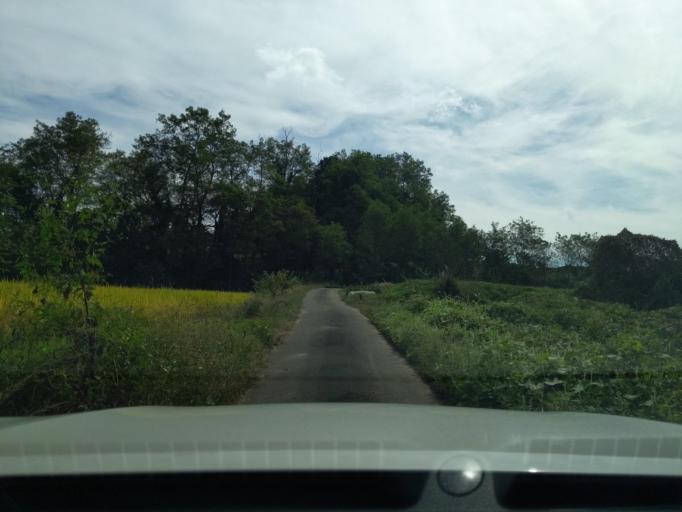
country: JP
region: Fukushima
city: Koriyama
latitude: 37.4133
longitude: 140.2996
